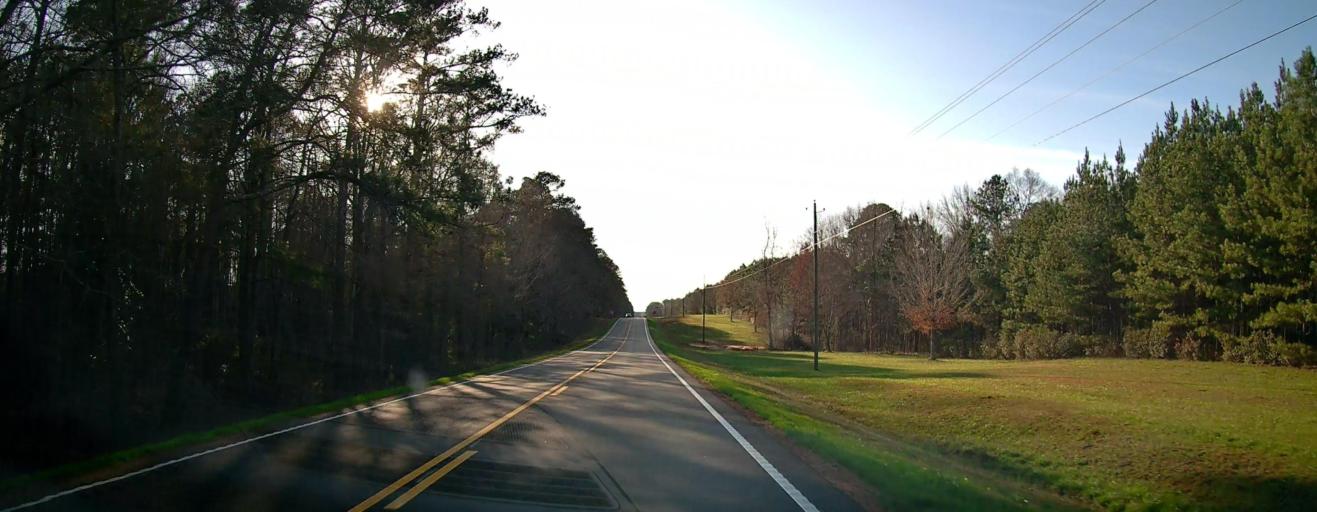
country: US
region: Georgia
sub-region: Harris County
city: Hamilton
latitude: 32.7473
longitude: -85.0041
